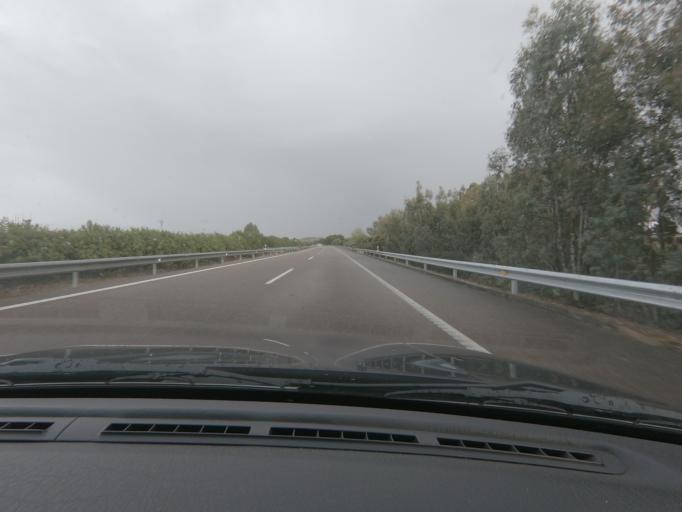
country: ES
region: Extremadura
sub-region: Provincia de Badajoz
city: Talavera La Real
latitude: 38.8693
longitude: -6.8487
